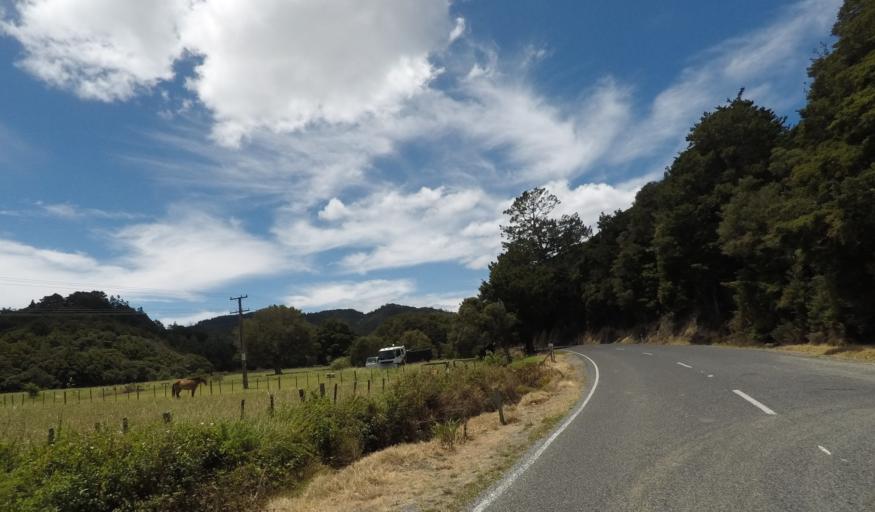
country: NZ
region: Northland
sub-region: Whangarei
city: Ngunguru
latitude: -35.5051
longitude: 174.4269
